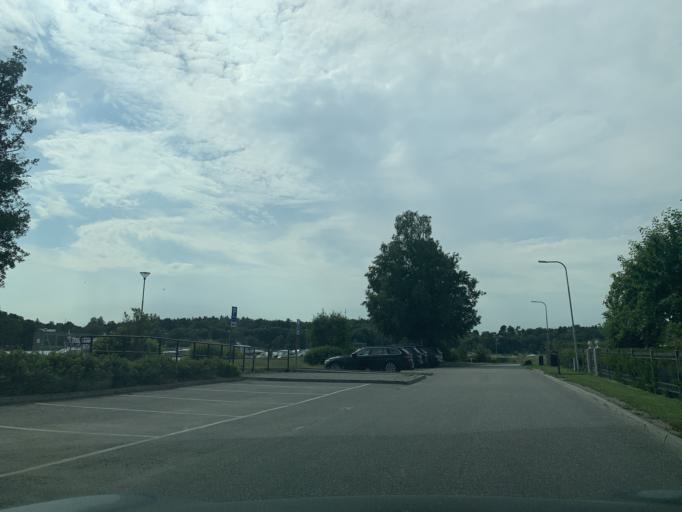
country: SE
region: Stockholm
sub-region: Norrtalje Kommun
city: Bergshamra
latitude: 59.3993
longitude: 18.0149
